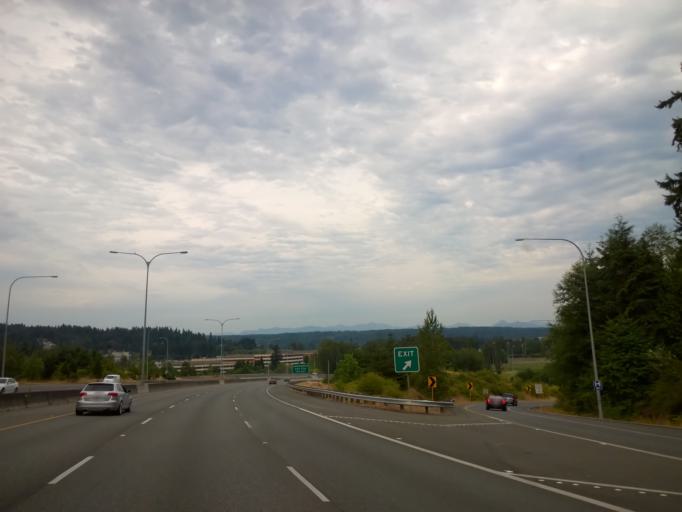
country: US
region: Washington
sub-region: King County
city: Redmond
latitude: 47.6666
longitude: -122.1291
